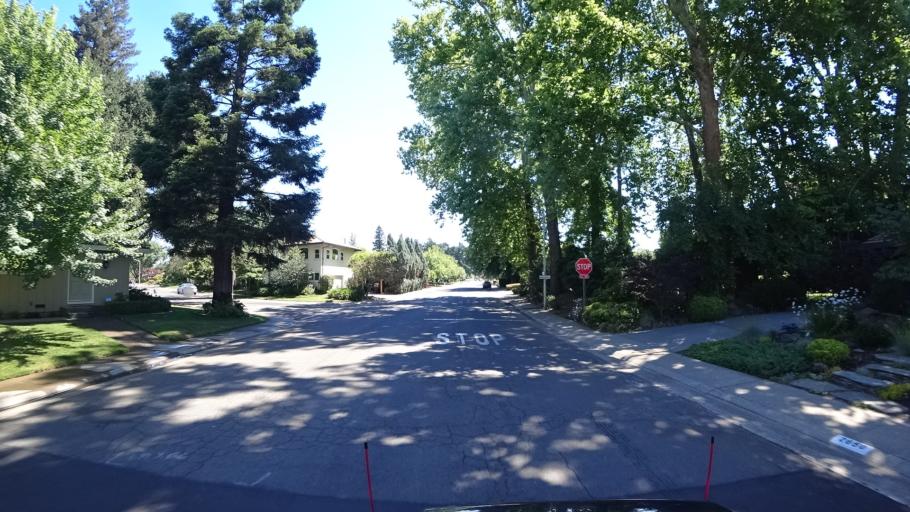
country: US
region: California
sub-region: Sacramento County
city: Rosemont
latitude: 38.5641
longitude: -121.3994
